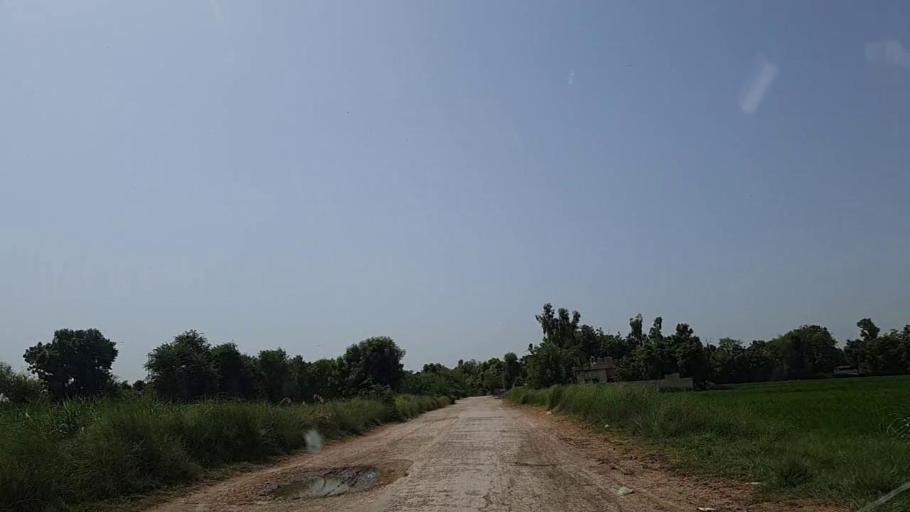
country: PK
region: Sindh
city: Naushahro Firoz
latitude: 26.8320
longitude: 68.0200
